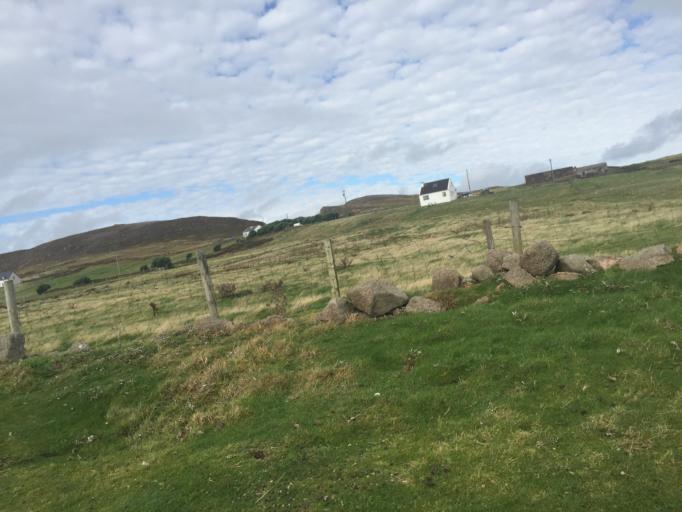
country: IE
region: Ulster
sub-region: County Donegal
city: Derrybeg
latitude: 55.2545
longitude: -8.1982
